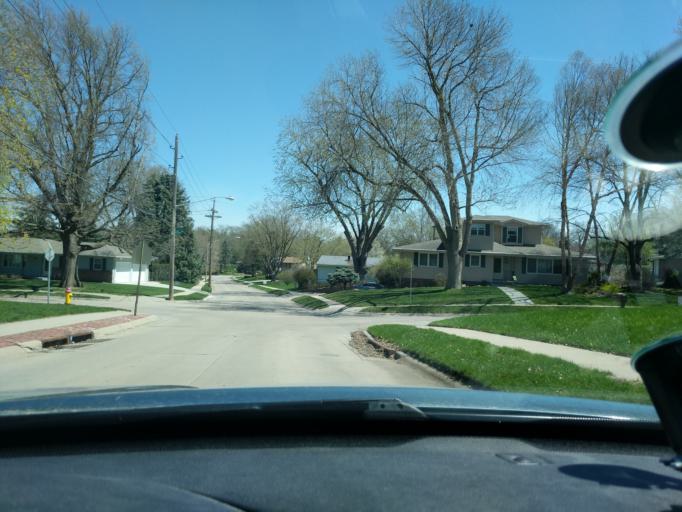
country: US
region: Nebraska
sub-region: Douglas County
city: Ralston
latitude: 41.2268
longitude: -96.0969
